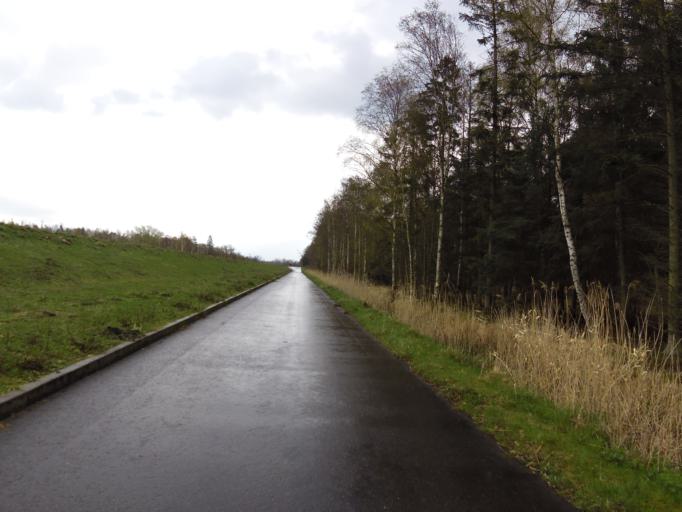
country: DE
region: Mecklenburg-Vorpommern
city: Barth
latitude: 54.4352
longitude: 12.7872
